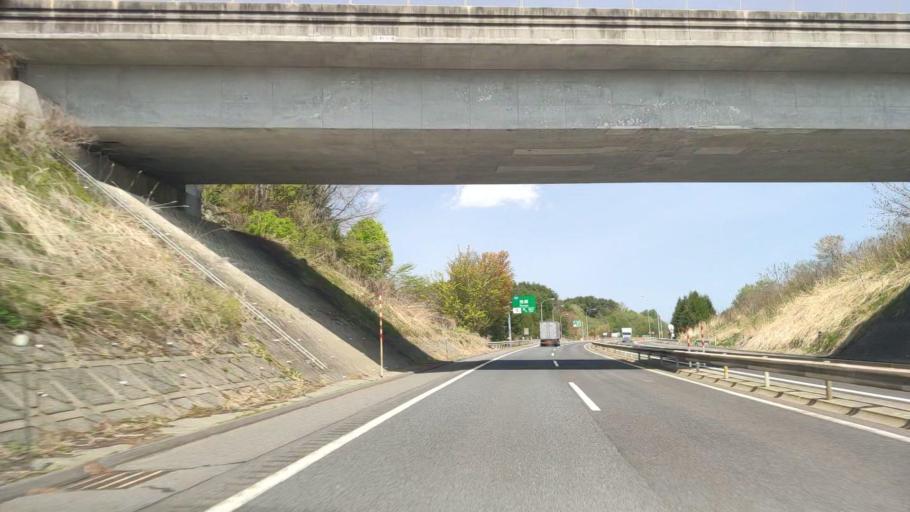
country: JP
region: Aomori
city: Hachinohe
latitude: 40.4031
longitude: 141.4437
